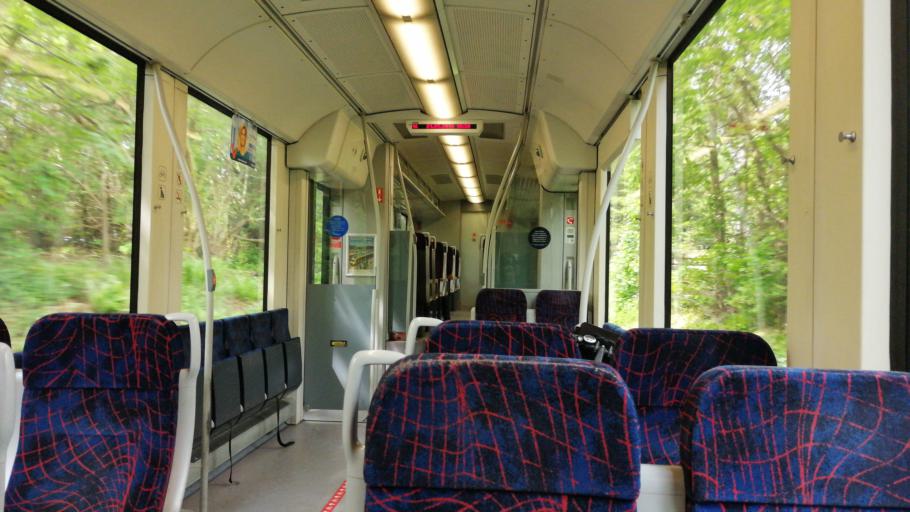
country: DK
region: Capital Region
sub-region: Gribskov Kommune
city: Gilleleje
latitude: 56.0983
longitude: 12.3758
